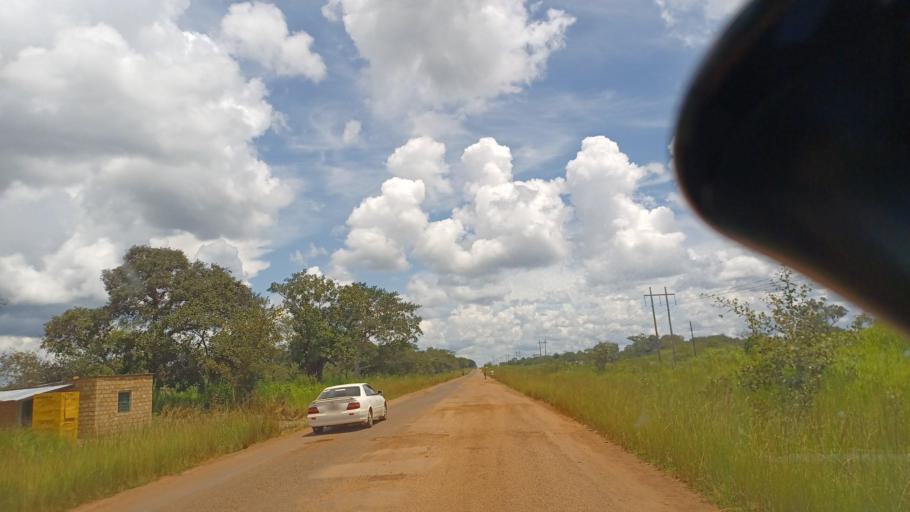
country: ZM
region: North-Western
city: Solwezi
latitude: -12.4835
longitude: 26.1963
